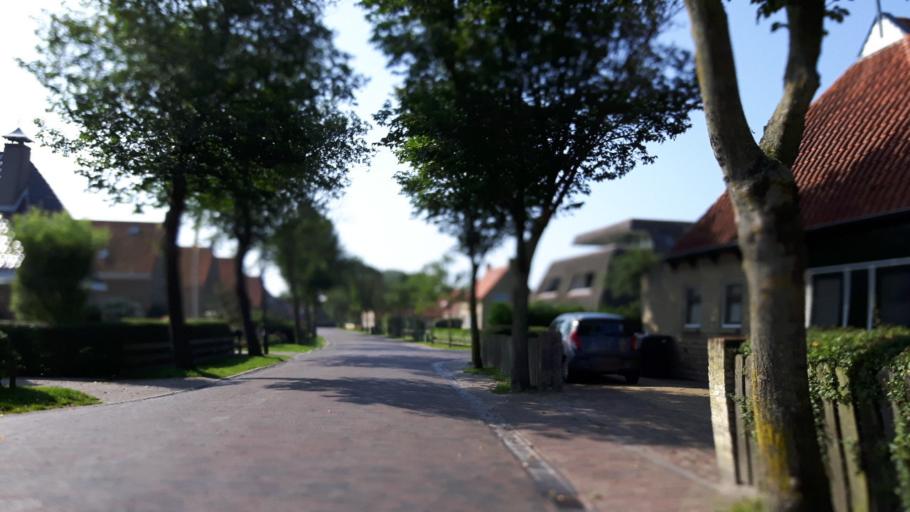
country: NL
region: Friesland
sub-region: Gemeente Ameland
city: Nes
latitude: 53.4492
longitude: 5.8001
